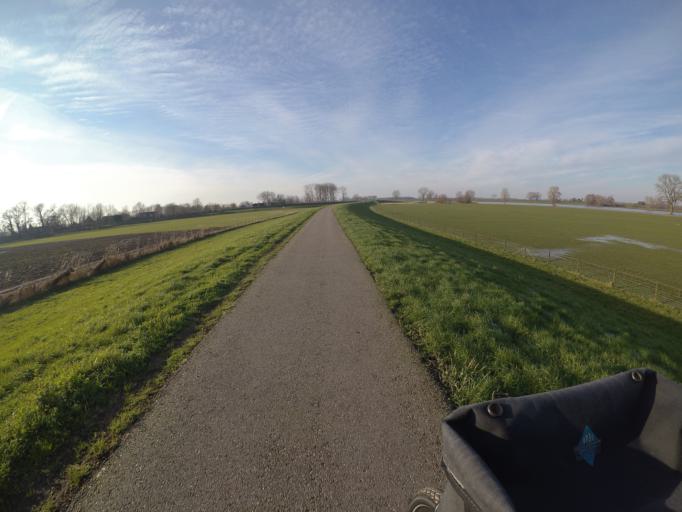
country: NL
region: Gelderland
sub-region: Gemeente Zaltbommel
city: Nederhemert-Noord
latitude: 51.7384
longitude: 5.1892
